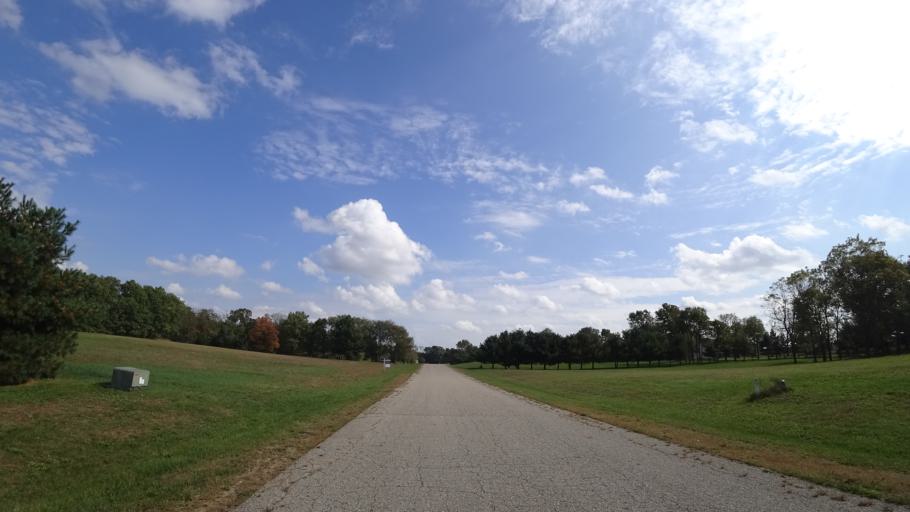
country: US
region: Michigan
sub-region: Saint Joseph County
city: Three Rivers
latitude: 41.9267
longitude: -85.6109
